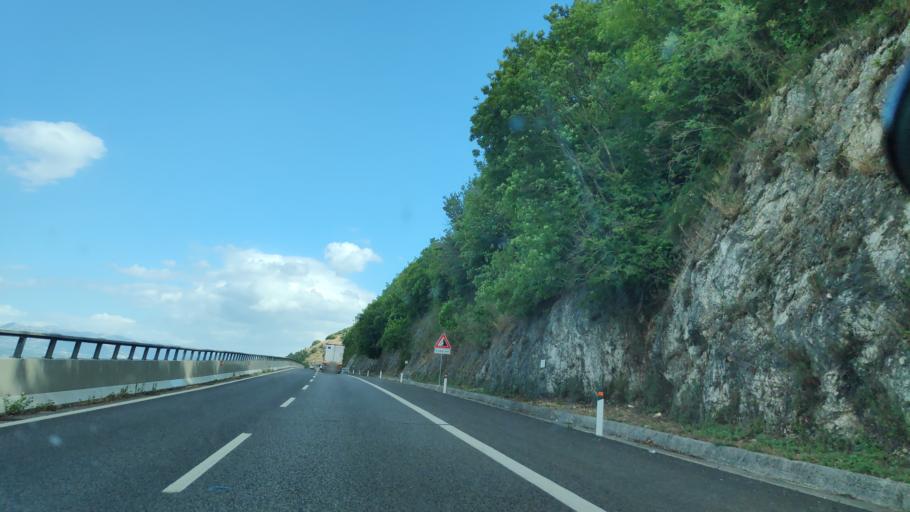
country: IT
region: Campania
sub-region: Provincia di Salerno
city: Sicignano degli Alburni
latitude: 40.5879
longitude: 15.3350
